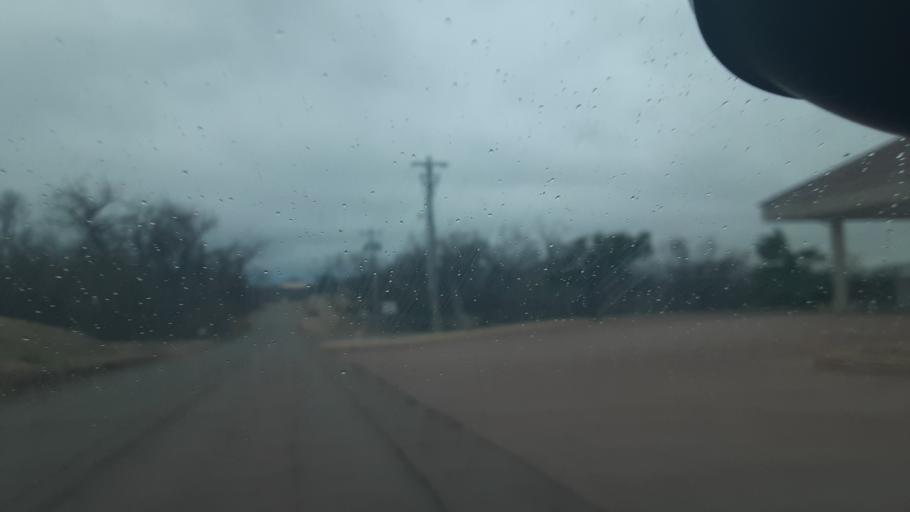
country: US
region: Oklahoma
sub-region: Logan County
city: Guthrie
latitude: 35.8780
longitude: -97.4014
